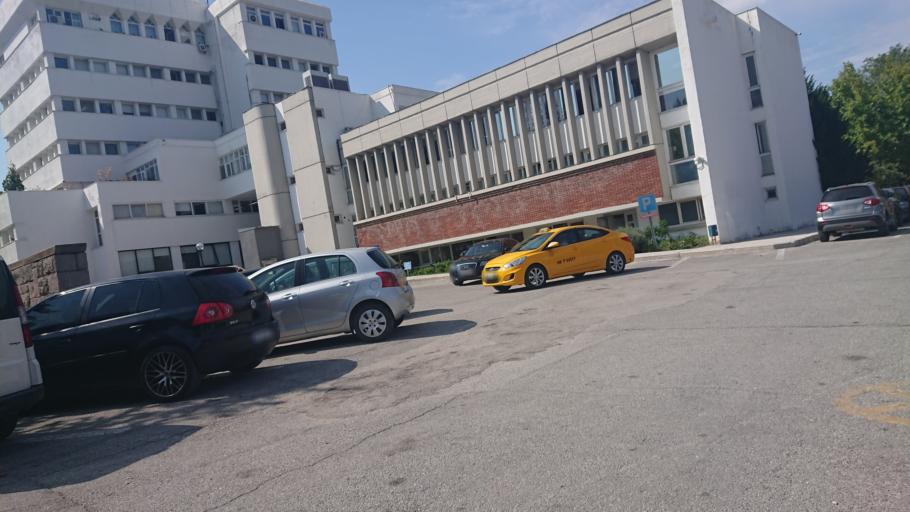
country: TR
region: Ankara
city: Ankara
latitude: 39.8945
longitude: 32.7847
